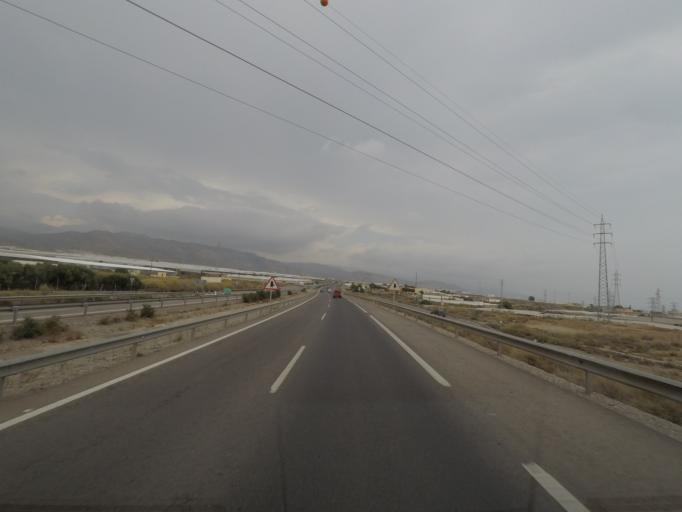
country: ES
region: Andalusia
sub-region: Provincia de Almeria
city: Vicar
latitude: 36.7957
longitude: -2.6852
